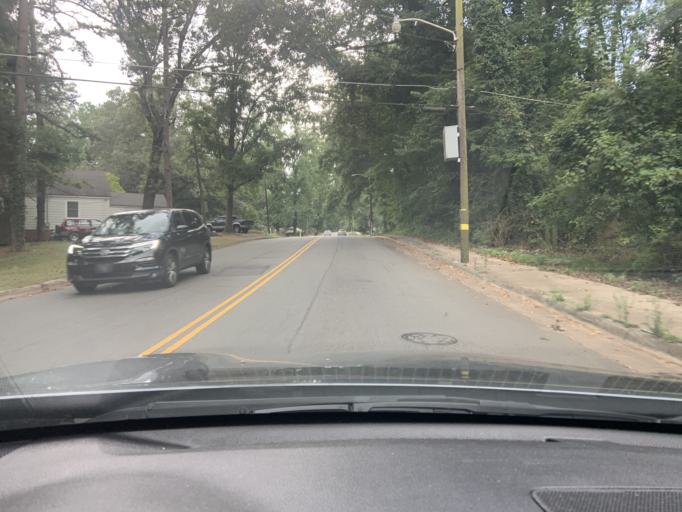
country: US
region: North Carolina
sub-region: Mecklenburg County
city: Charlotte
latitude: 35.2309
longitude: -80.8842
